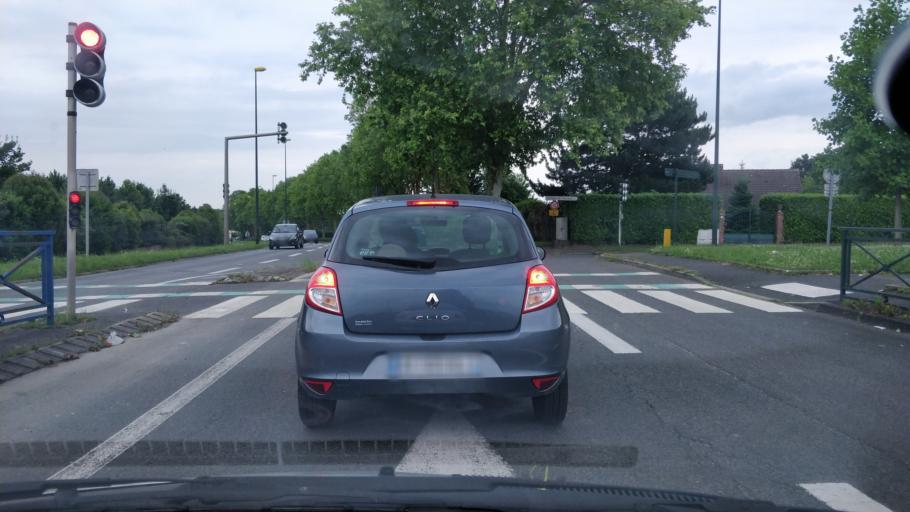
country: FR
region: Ile-de-France
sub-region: Departement de Seine-et-Marne
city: Chelles
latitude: 48.8893
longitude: 2.5988
